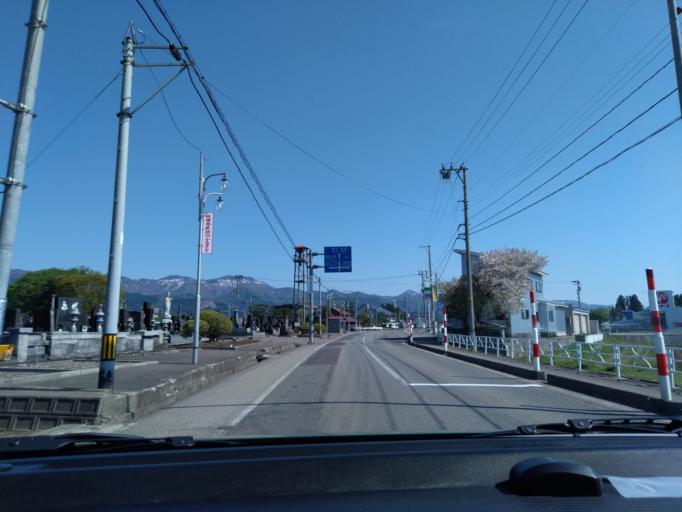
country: JP
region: Akita
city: Kakunodatemachi
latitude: 39.5085
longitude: 140.5952
